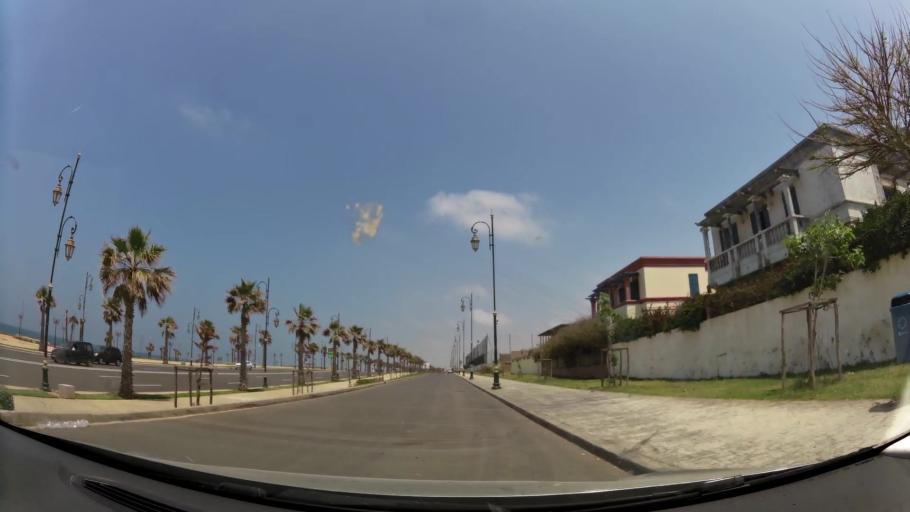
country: MA
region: Rabat-Sale-Zemmour-Zaer
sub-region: Skhirate-Temara
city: Temara
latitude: 33.9713
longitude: -6.9039
